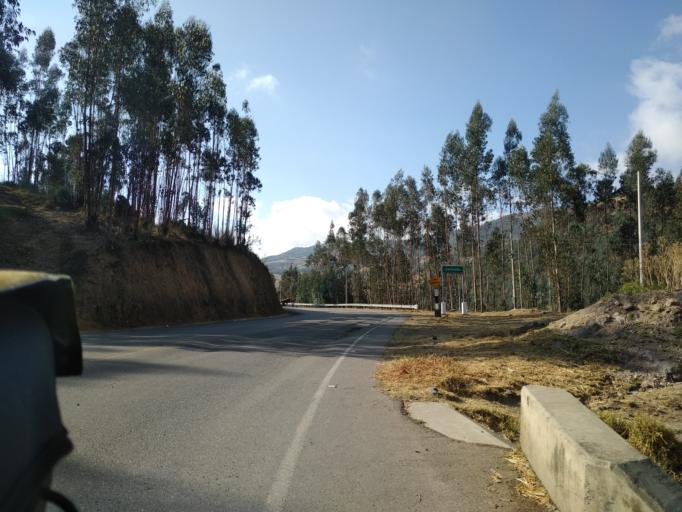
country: PE
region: La Libertad
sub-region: Provincia de Otuzco
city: Agallpampa
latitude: -7.9971
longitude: -78.5085
